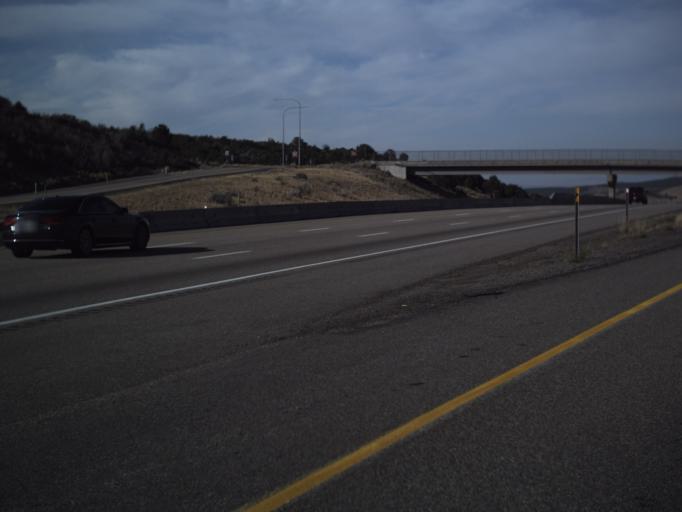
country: US
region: Utah
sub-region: Millard County
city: Fillmore
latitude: 39.2040
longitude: -112.1711
